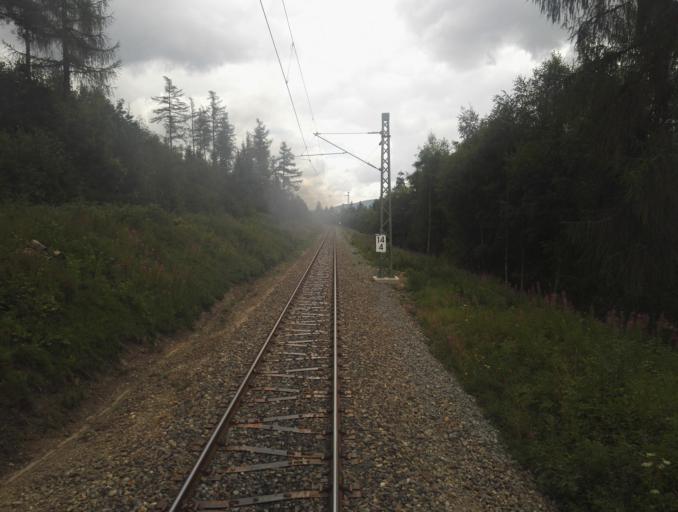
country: DE
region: Baden-Wuerttemberg
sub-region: Freiburg Region
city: Schluchsee
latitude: 47.8272
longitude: 8.1458
